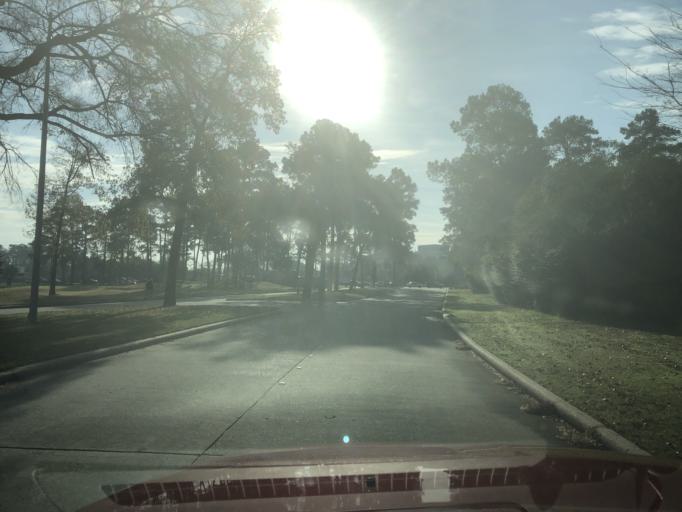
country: US
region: Texas
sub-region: Harris County
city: Spring
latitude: 30.0035
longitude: -95.4735
